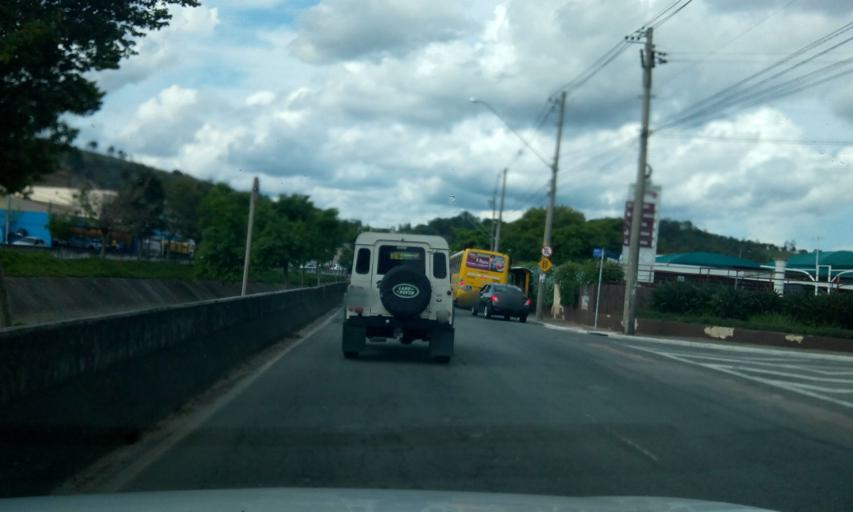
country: BR
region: Sao Paulo
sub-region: Jundiai
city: Jundiai
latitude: -23.1723
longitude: -46.8933
